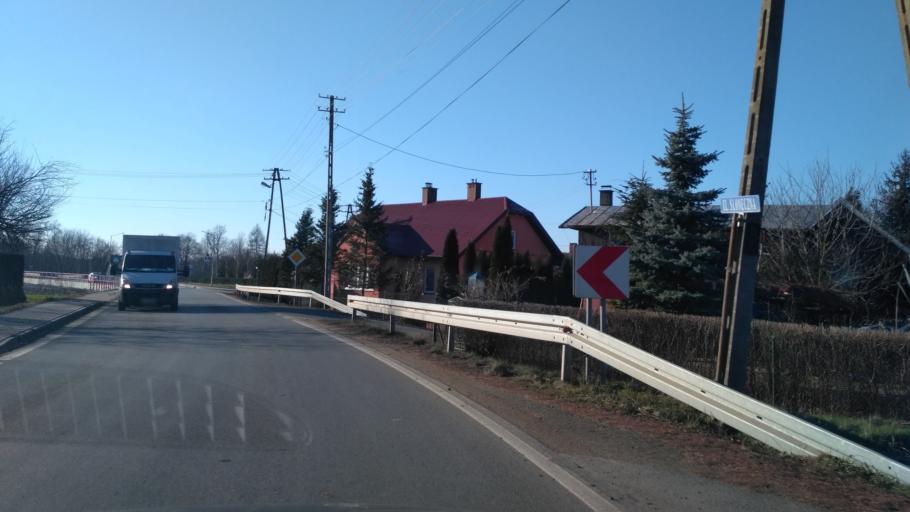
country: PL
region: Subcarpathian Voivodeship
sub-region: Powiat brzozowski
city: Haczow
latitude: 49.6792
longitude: 21.8671
